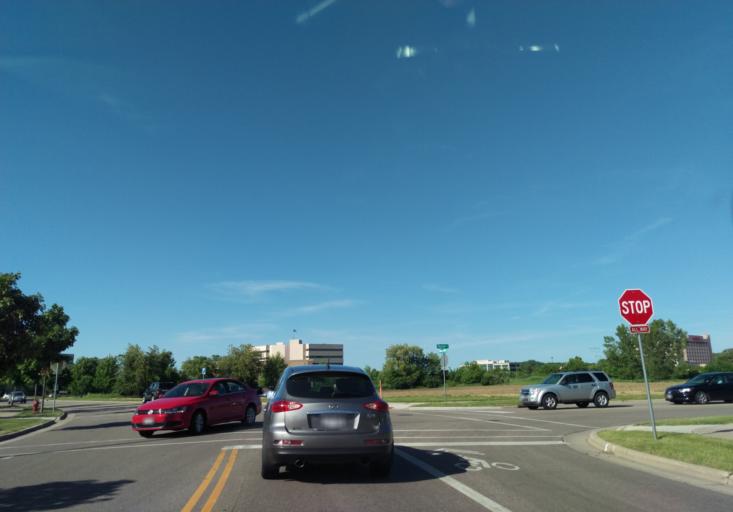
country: US
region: Wisconsin
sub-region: Dane County
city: Middleton
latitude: 43.0858
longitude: -89.5286
